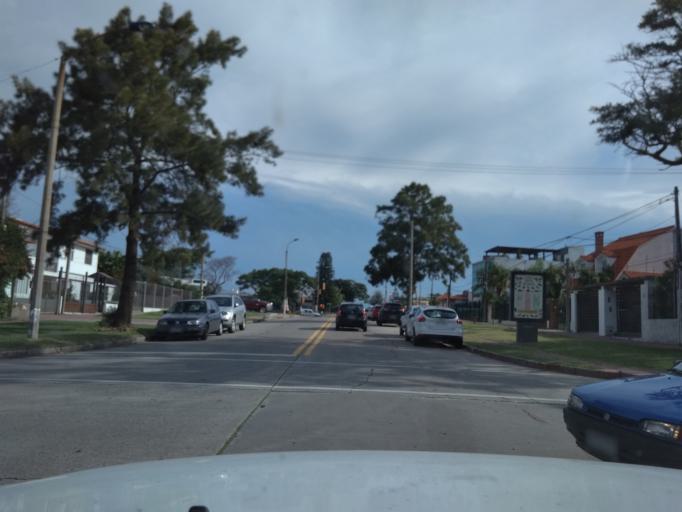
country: UY
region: Canelones
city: Paso de Carrasco
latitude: -34.8951
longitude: -56.0803
